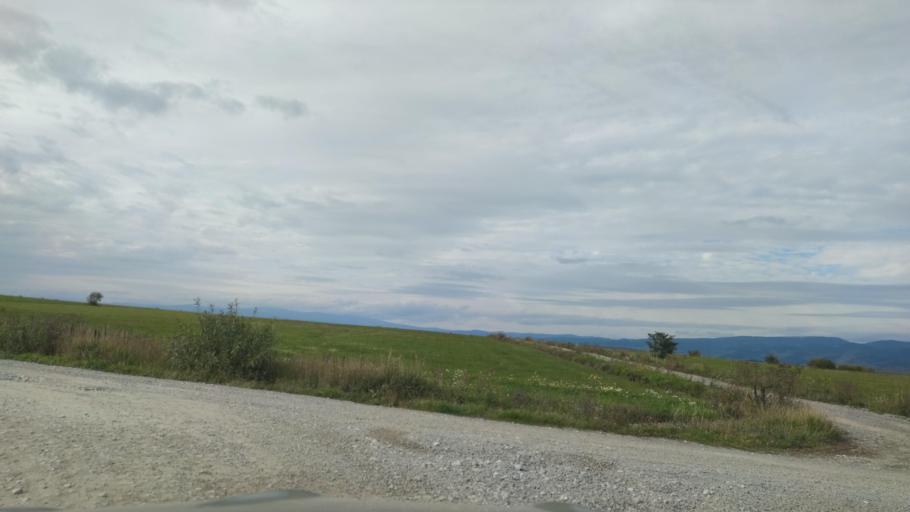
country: RO
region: Harghita
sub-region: Comuna Remetea
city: Remetea
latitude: 46.8164
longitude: 25.4219
